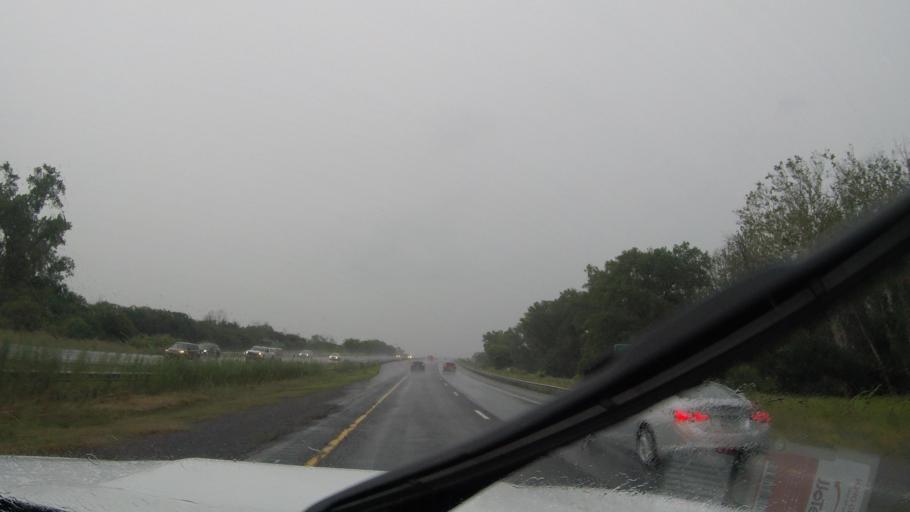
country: US
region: New York
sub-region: Seneca County
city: Bridgeport
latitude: 42.9965
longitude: -76.7361
